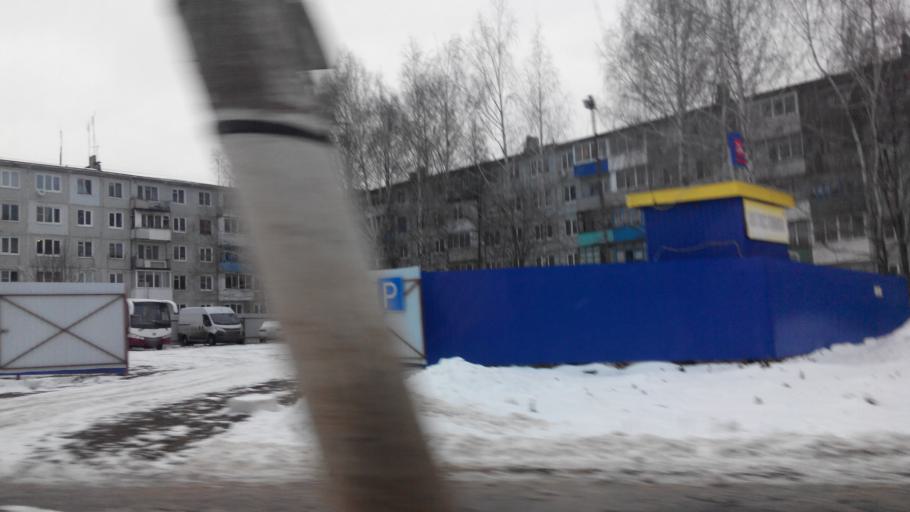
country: RU
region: Tula
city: Podlesnyy
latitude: 53.9669
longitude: 38.2868
